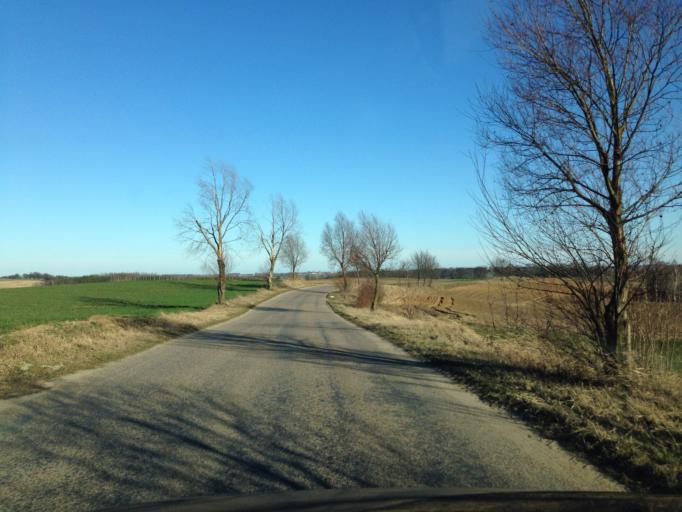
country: PL
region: Kujawsko-Pomorskie
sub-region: Powiat brodnicki
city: Brzozie
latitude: 53.2876
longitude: 19.6544
